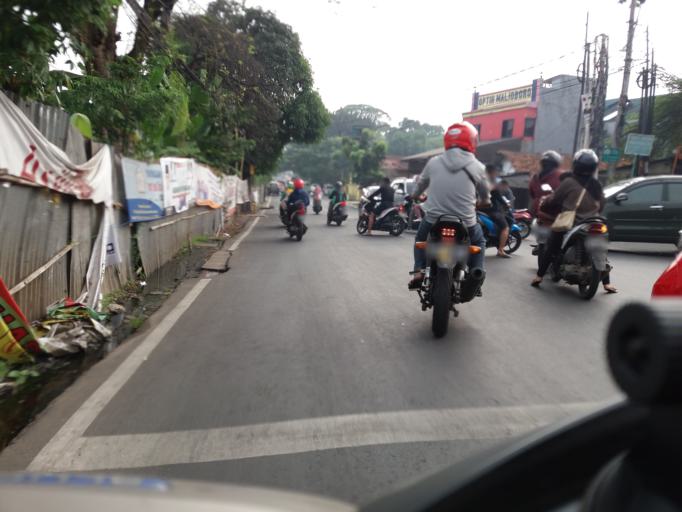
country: ID
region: West Java
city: Depok
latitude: -6.4053
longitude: 106.8503
